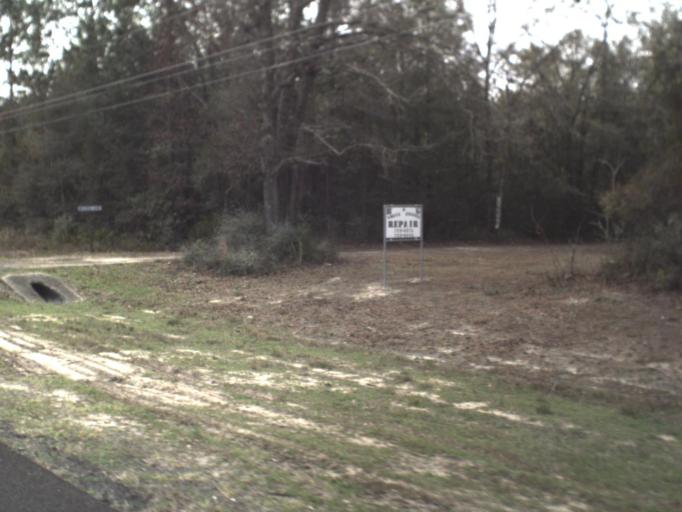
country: US
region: Florida
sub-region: Bay County
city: Youngstown
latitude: 30.4031
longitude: -85.4337
